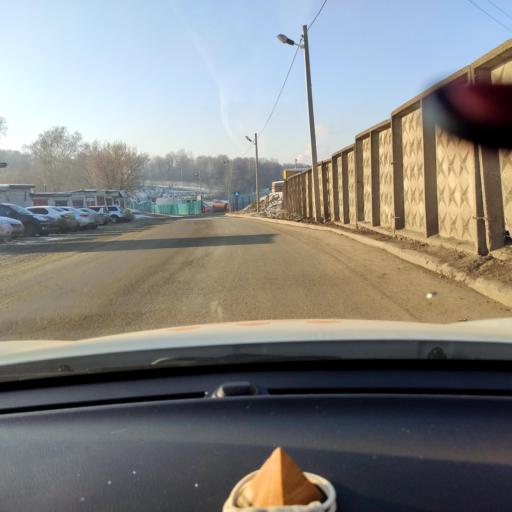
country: RU
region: Tatarstan
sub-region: Gorod Kazan'
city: Kazan
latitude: 55.8135
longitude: 49.0522
